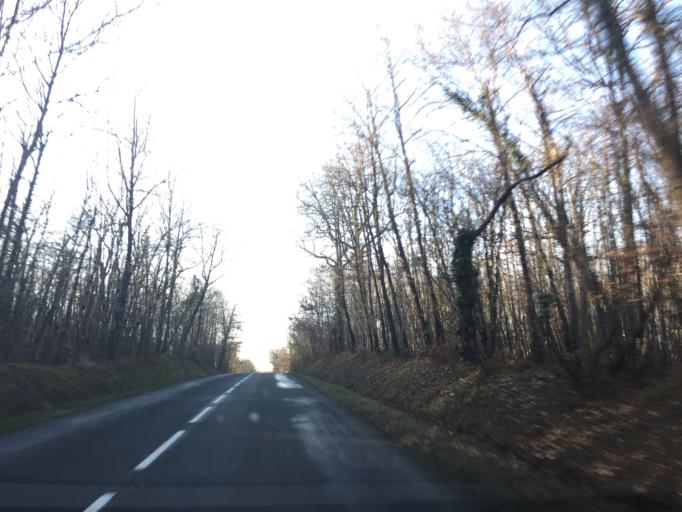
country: FR
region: Poitou-Charentes
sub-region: Departement de la Charente
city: Chalais
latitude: 45.2782
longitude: 0.1088
